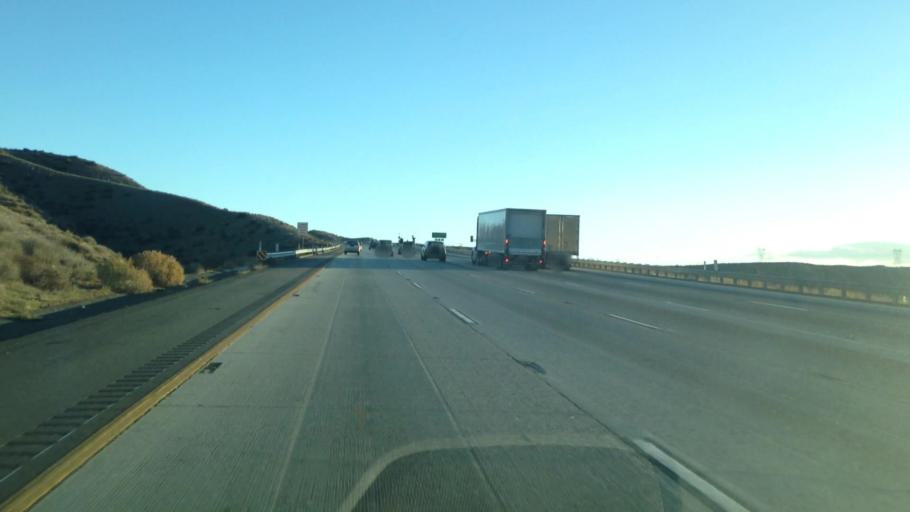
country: US
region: California
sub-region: San Bernardino County
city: Oak Hills
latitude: 34.3441
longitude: -117.4490
